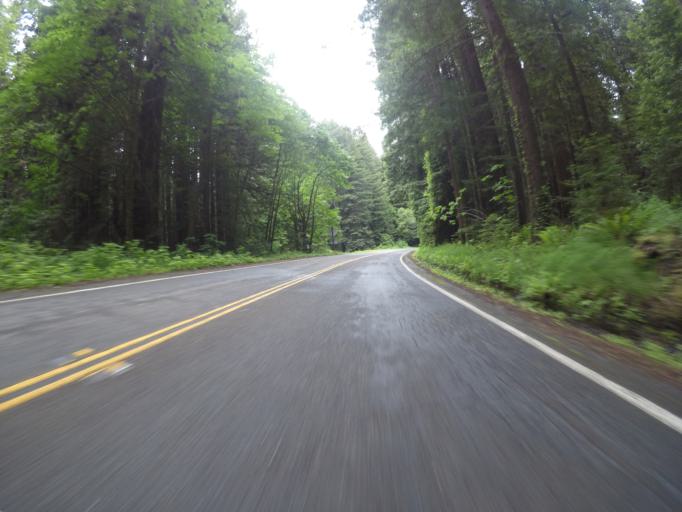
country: US
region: California
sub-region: Humboldt County
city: Rio Dell
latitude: 40.4459
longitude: -124.0160
